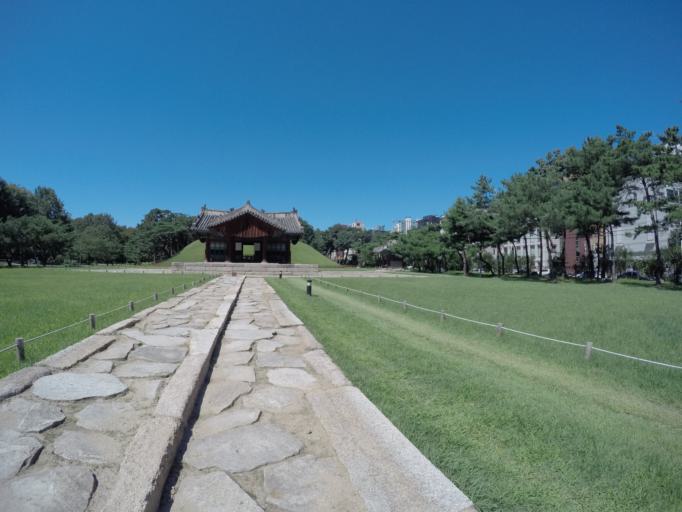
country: KR
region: Seoul
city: Seoul
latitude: 37.5081
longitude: 127.0529
